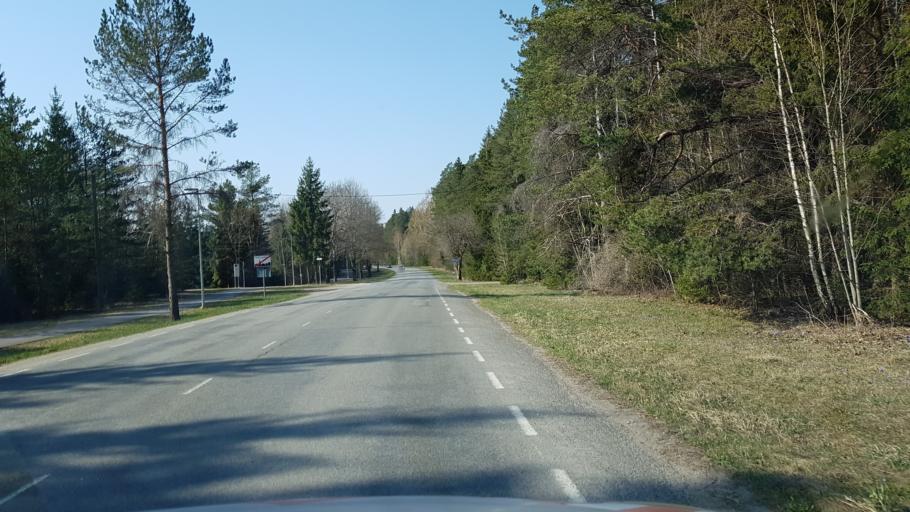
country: EE
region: Raplamaa
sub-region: Maerjamaa vald
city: Marjamaa
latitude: 58.8953
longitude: 24.4086
